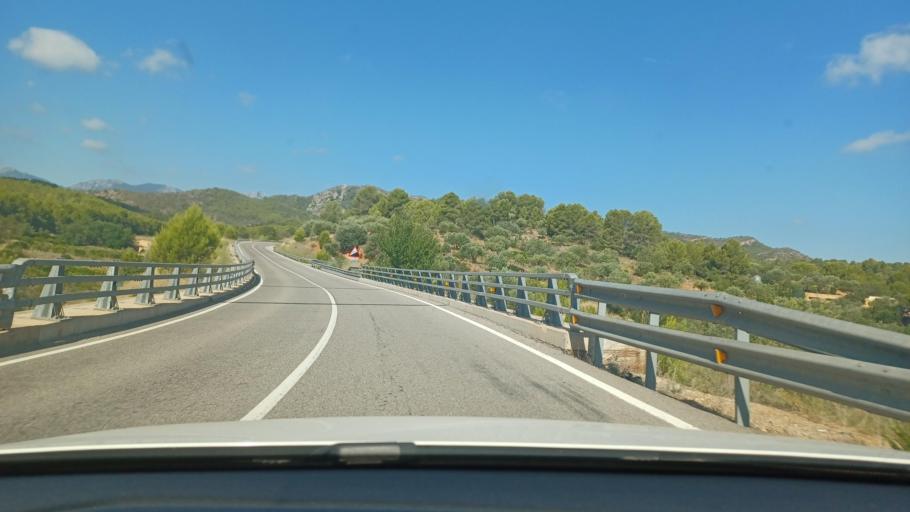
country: ES
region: Catalonia
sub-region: Provincia de Tarragona
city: Tivenys
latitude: 40.9344
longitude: 0.4785
